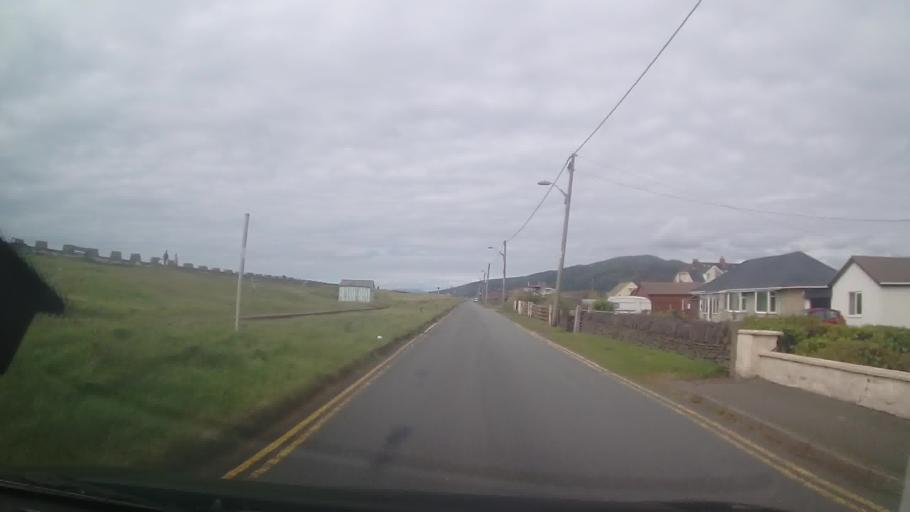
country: GB
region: Wales
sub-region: Gwynedd
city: Barmouth
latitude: 52.6977
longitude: -4.0567
